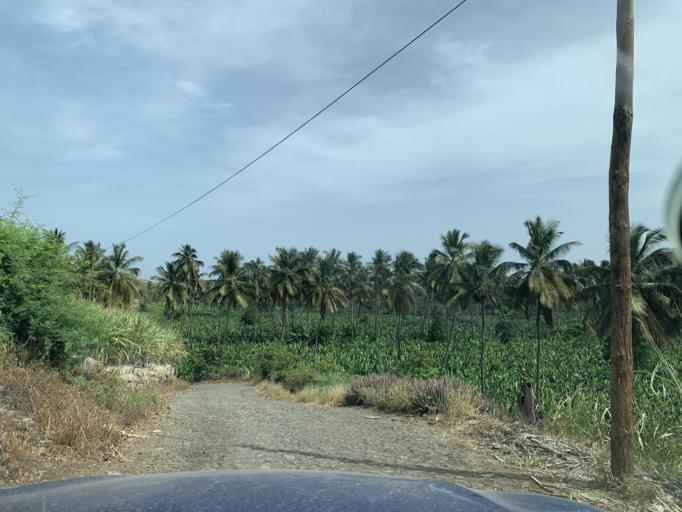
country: CV
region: Santa Cruz
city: Pedra Badejo
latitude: 15.1272
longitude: -23.5405
